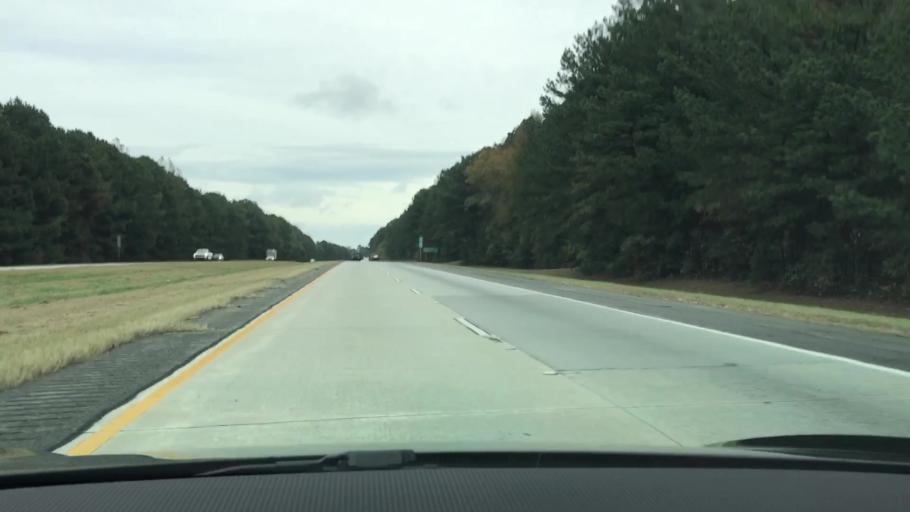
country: US
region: Georgia
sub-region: Greene County
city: Union Point
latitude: 33.5471
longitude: -83.0660
